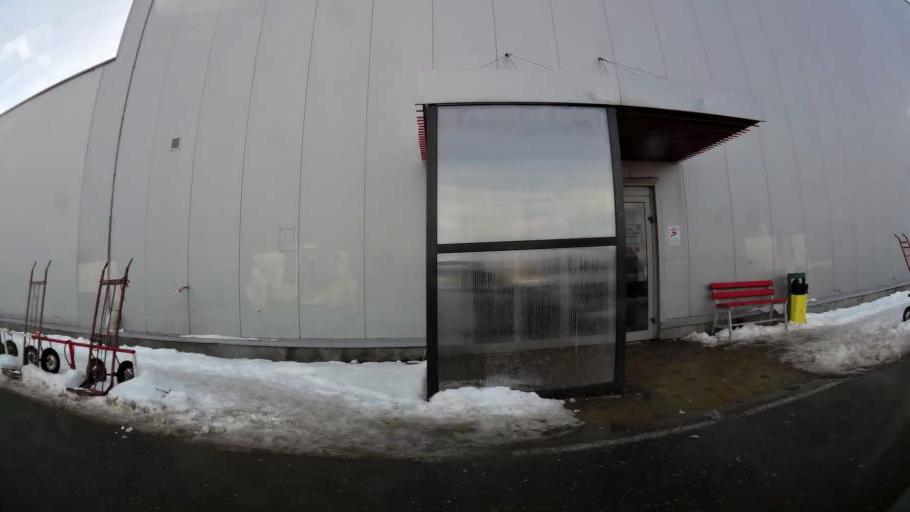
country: RO
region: Ilfov
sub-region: Voluntari City
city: Voluntari
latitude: 44.4777
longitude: 26.1864
